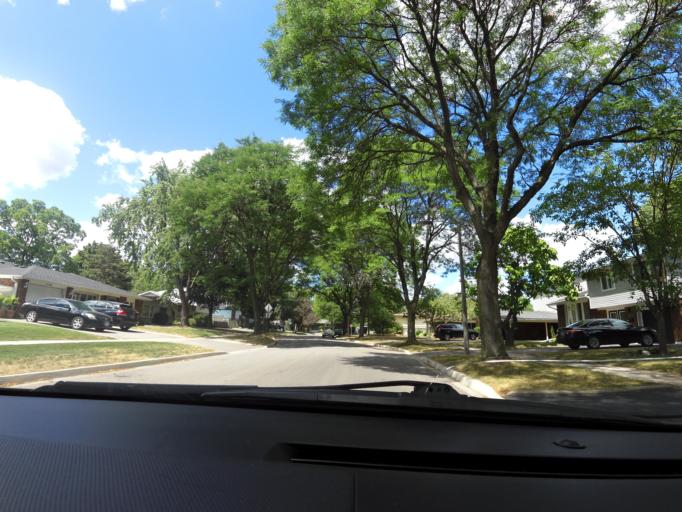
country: CA
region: Ontario
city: Burlington
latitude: 43.3545
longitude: -79.7736
